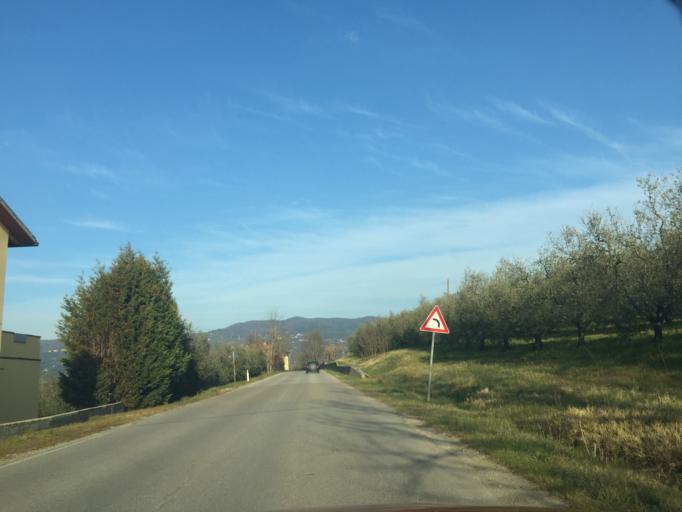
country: IT
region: Tuscany
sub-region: Province of Florence
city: Vinci
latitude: 43.7728
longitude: 10.9063
